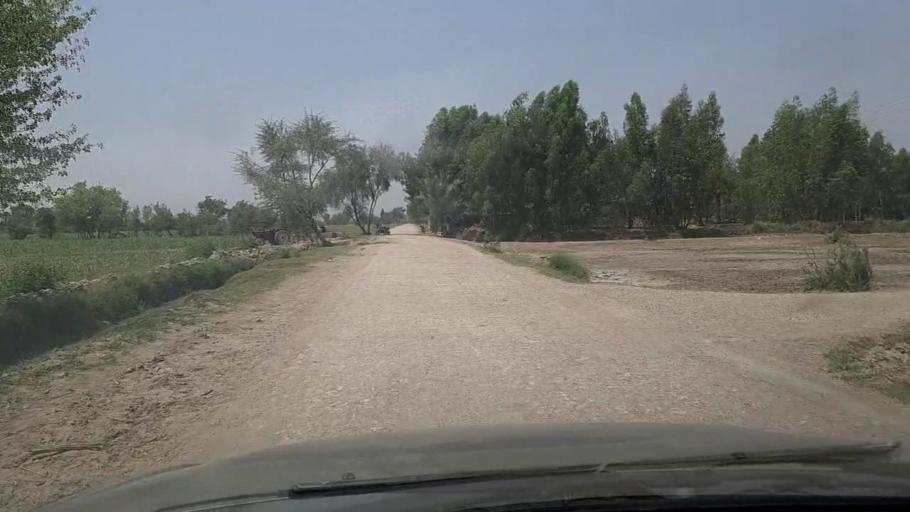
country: PK
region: Sindh
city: Adilpur
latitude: 27.9305
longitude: 69.2485
